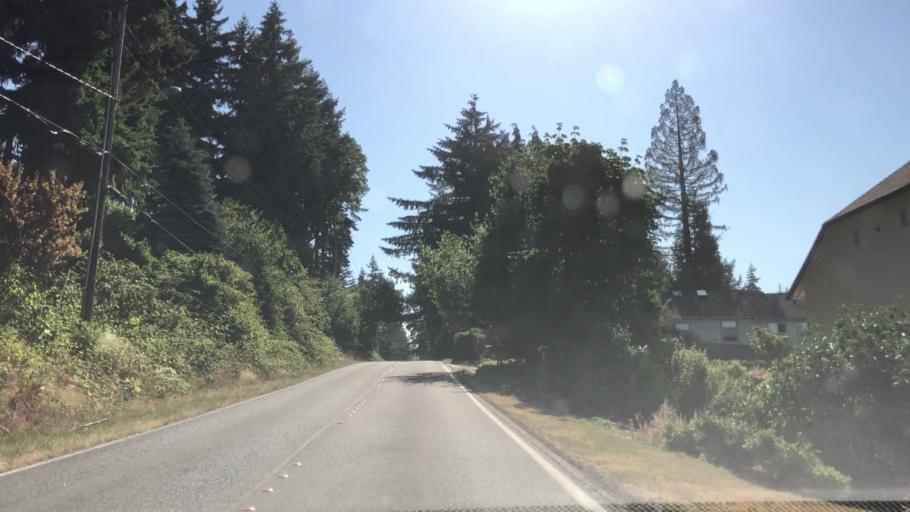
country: US
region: Washington
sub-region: King County
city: Eastgate
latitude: 47.6152
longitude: -122.1378
